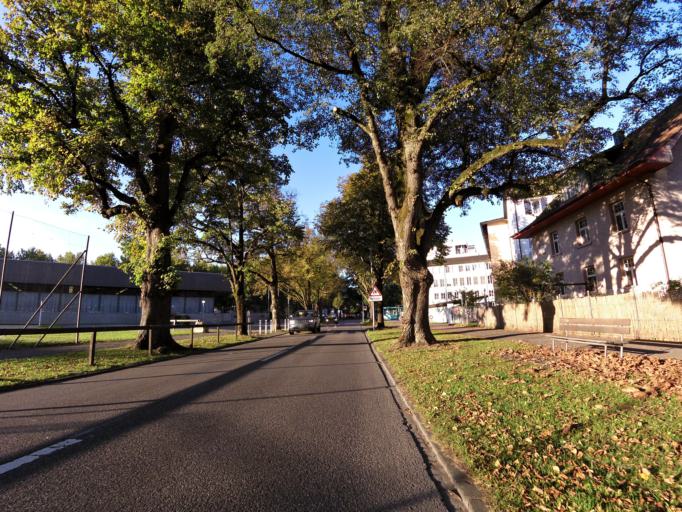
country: CH
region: Aargau
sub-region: Bezirk Aarau
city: Aarau
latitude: 47.3893
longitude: 8.0402
